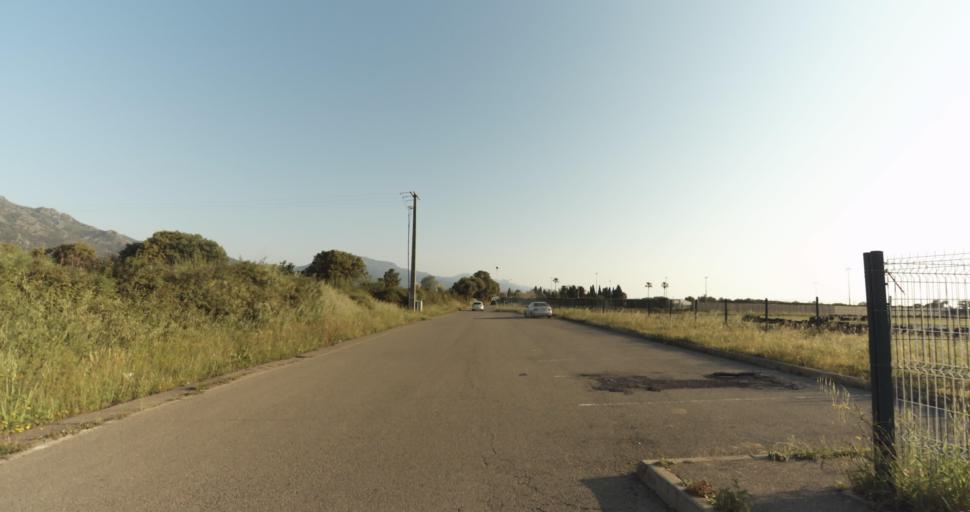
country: FR
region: Corsica
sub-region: Departement de la Haute-Corse
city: Biguglia
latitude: 42.6064
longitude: 9.4441
